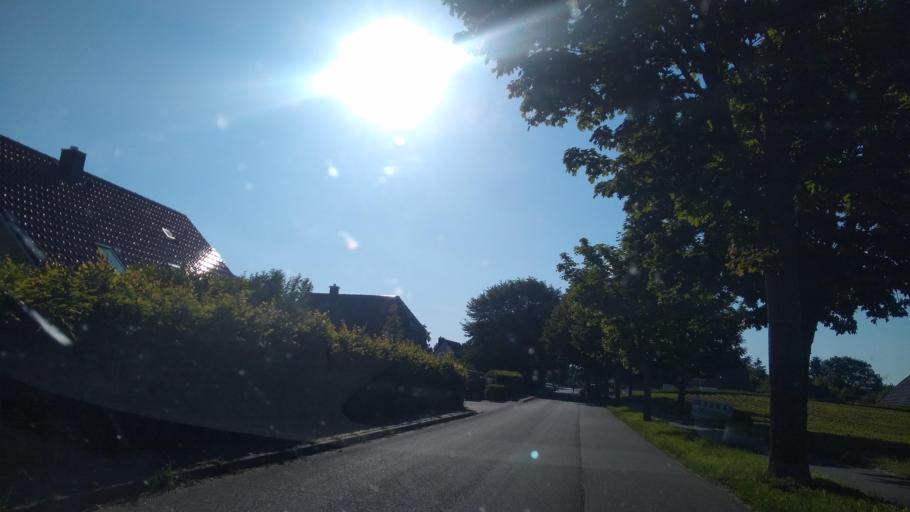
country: DE
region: Schleswig-Holstein
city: Neudorf-Bornstein
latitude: 54.4179
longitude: 9.9237
